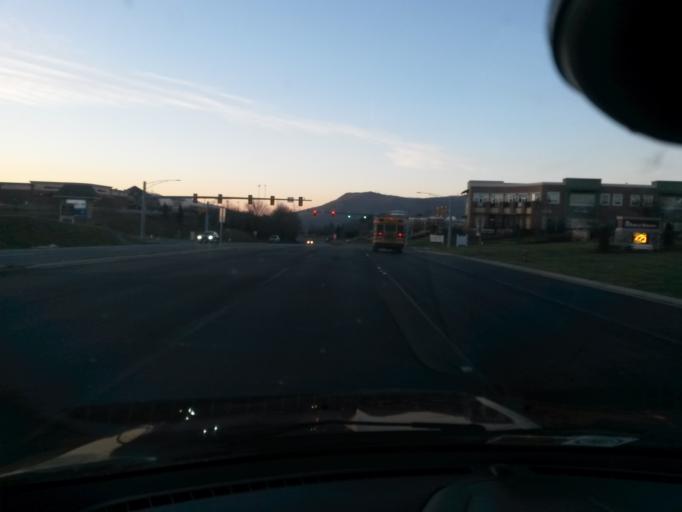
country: US
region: Virginia
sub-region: Botetourt County
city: Daleville
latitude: 37.4177
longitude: -79.9118
